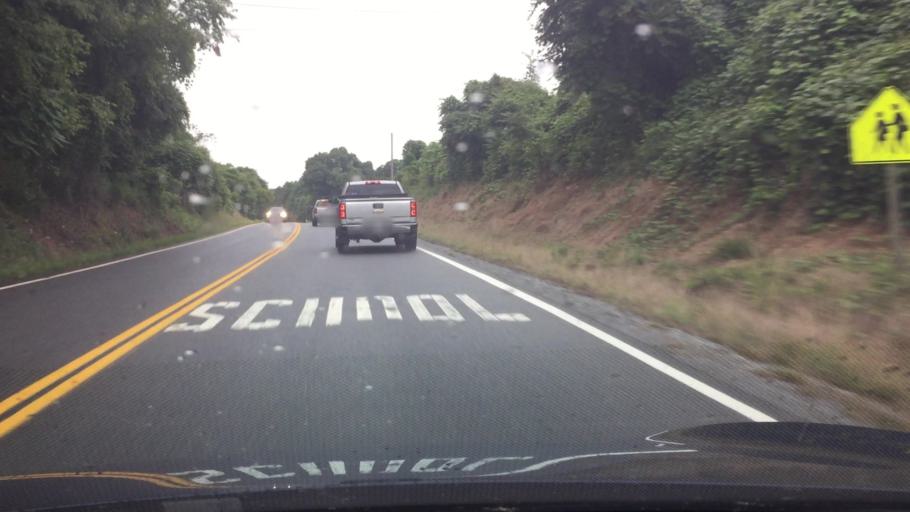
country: US
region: Virginia
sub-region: City of Bedford
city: Bedford
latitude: 37.3657
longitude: -79.4303
